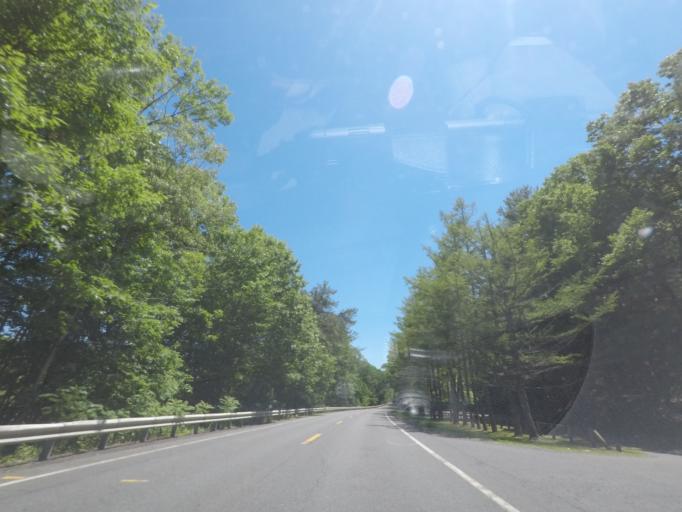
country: US
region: Massachusetts
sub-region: Hampshire County
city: Westhampton
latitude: 42.2441
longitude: -72.9168
